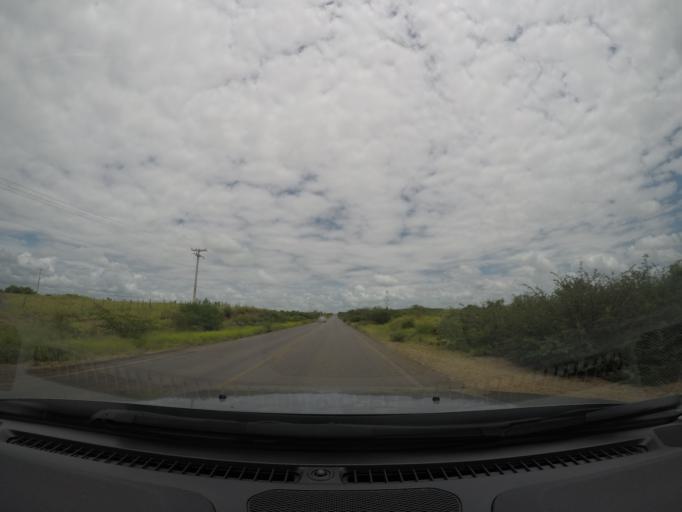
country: BR
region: Bahia
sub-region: Itaberaba
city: Itaberaba
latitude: -12.4858
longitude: -40.2213
